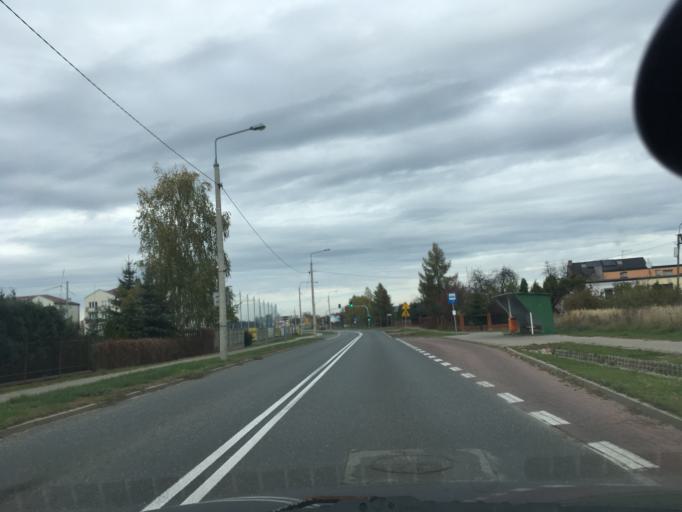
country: PL
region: Masovian Voivodeship
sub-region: Powiat zyrardowski
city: Mszczonow
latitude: 51.9755
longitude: 20.5296
